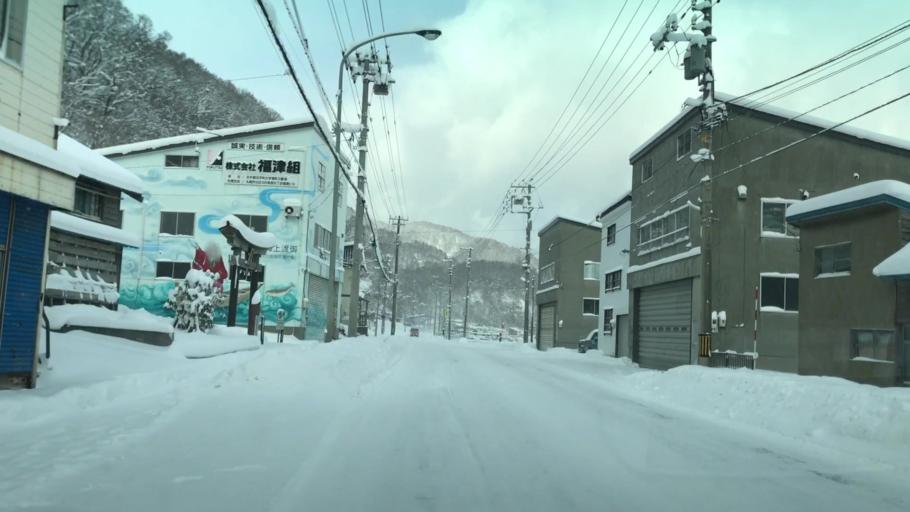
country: JP
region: Hokkaido
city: Yoichi
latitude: 43.2676
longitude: 140.6388
